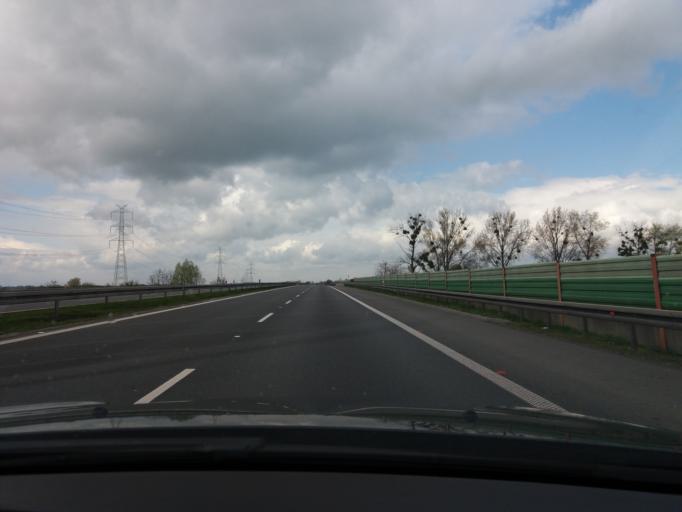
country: PL
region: Opole Voivodeship
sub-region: Powiat brzeski
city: Skarbimierz Osiedle
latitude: 50.8050
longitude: 17.3188
